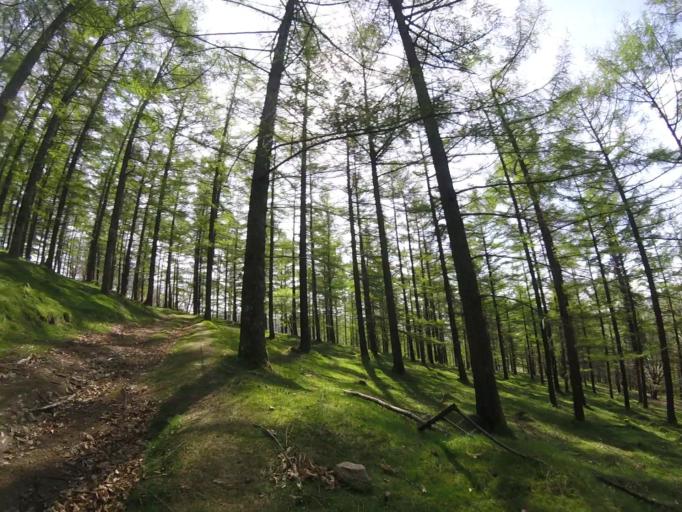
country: ES
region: Navarre
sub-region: Provincia de Navarra
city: Arano
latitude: 43.2550
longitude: -1.8300
